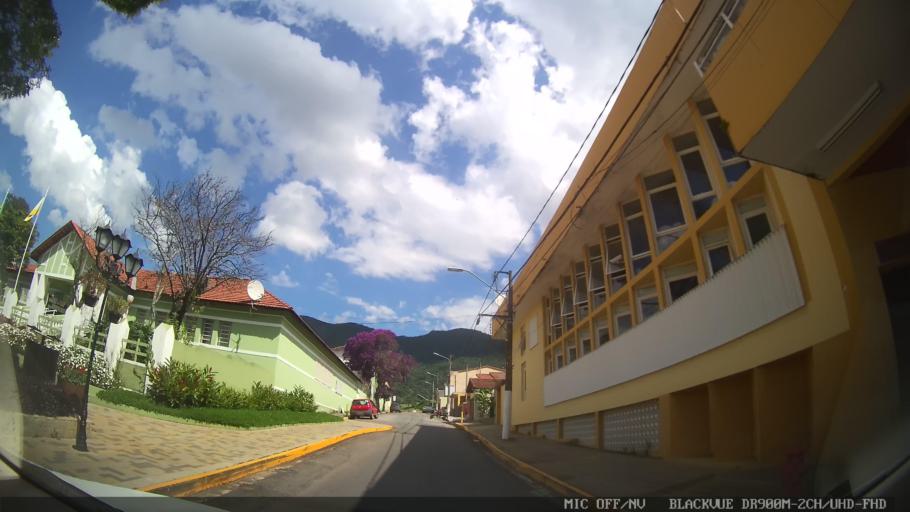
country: BR
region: Minas Gerais
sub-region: Extrema
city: Extrema
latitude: -22.8562
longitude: -46.3185
